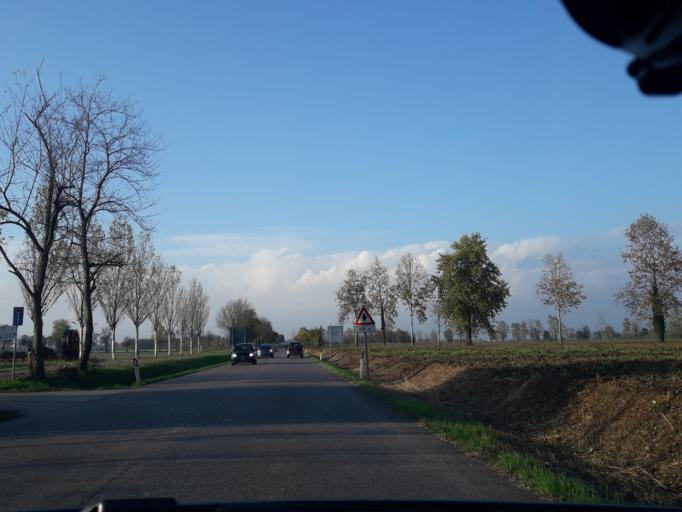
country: IT
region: Friuli Venezia Giulia
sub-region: Provincia di Udine
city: Pradamano
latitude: 46.0386
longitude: 13.2914
